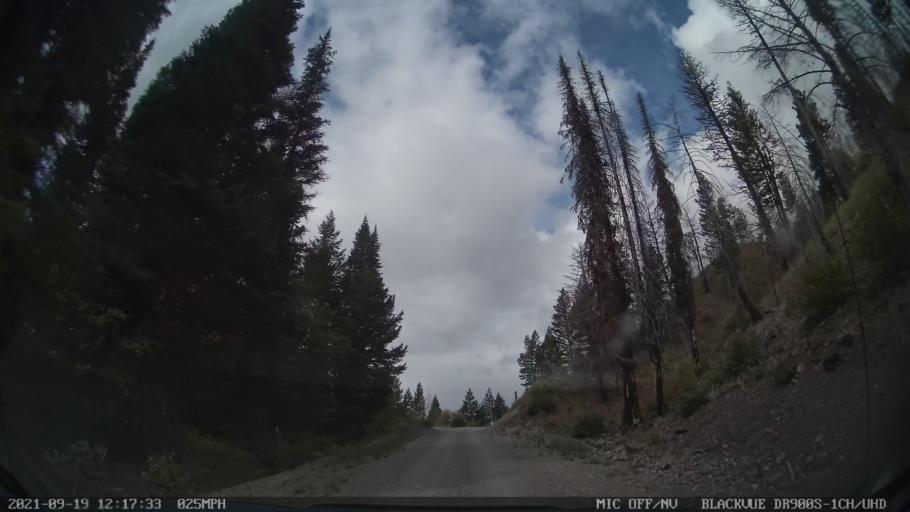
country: US
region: Montana
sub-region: Missoula County
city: Seeley Lake
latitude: 47.1721
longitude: -113.3595
